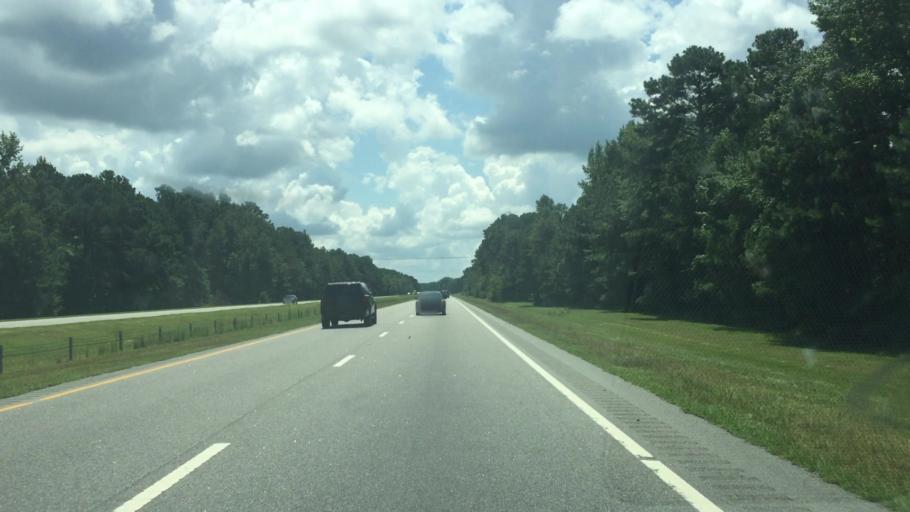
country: US
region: North Carolina
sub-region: Robeson County
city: Lumberton
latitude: 34.5404
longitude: -79.0202
